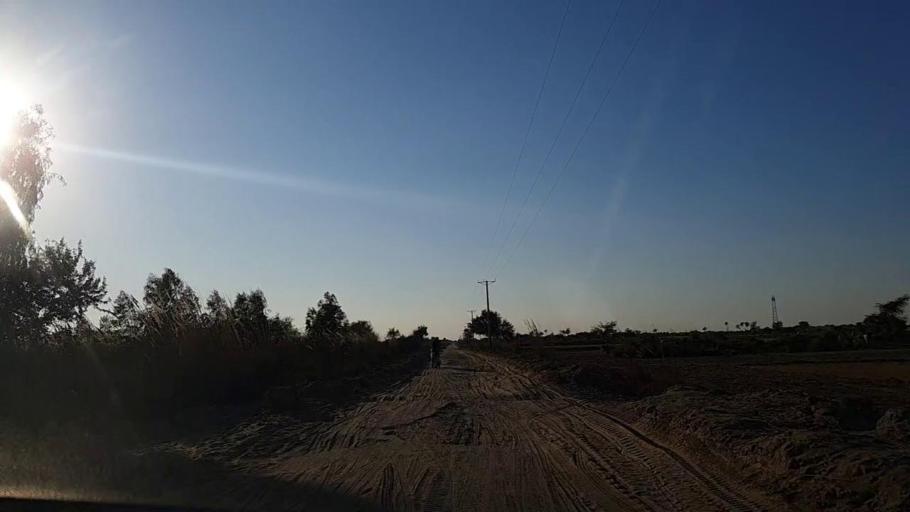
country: PK
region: Sindh
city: Khadro
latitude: 26.2790
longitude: 68.8800
